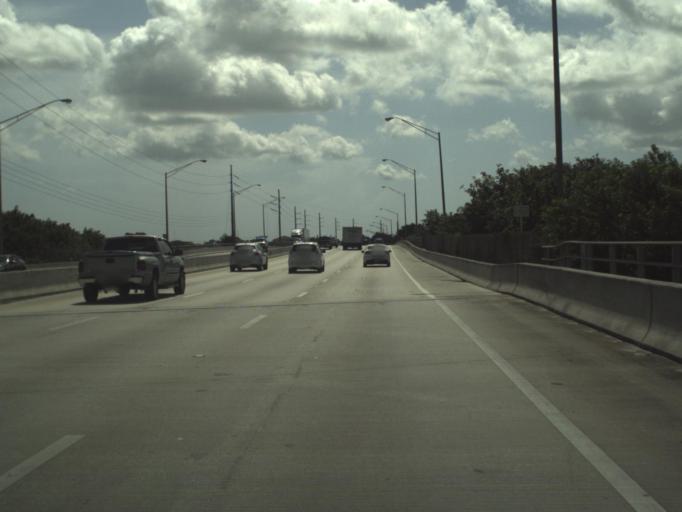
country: US
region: Florida
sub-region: Saint Lucie County
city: Port Saint Lucie
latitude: 27.2717
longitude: -80.3241
